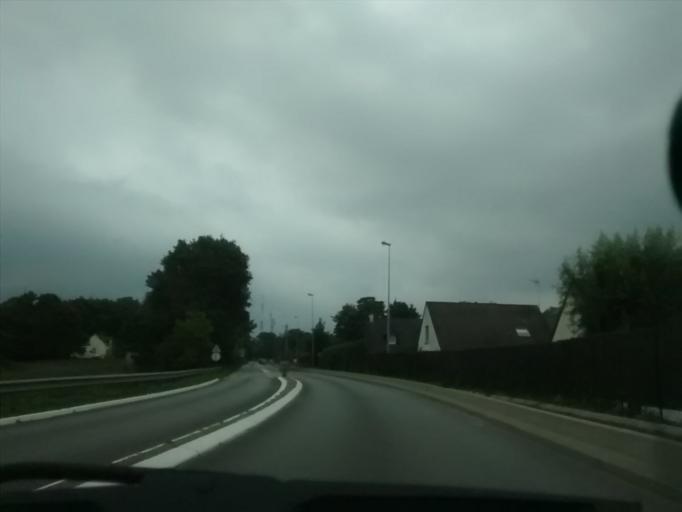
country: FR
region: Brittany
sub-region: Departement du Morbihan
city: Guer
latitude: 47.9119
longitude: -2.1236
